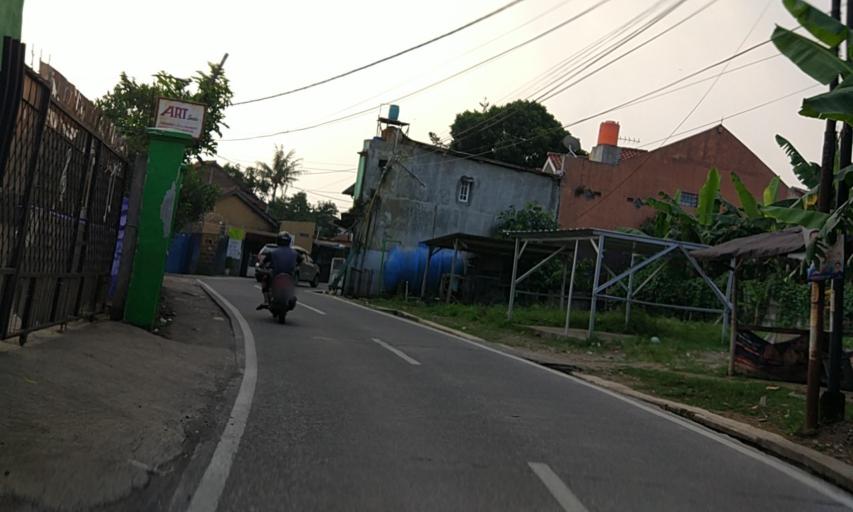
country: ID
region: West Java
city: Bandung
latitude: -6.9148
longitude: 107.6847
